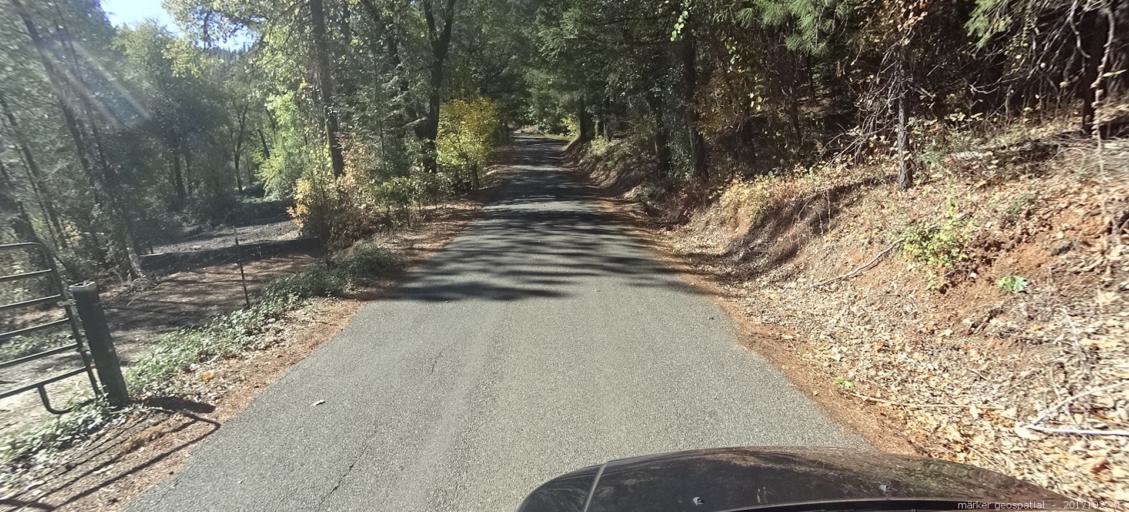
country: US
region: California
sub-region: Shasta County
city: Central Valley (historical)
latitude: 40.9343
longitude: -122.4606
